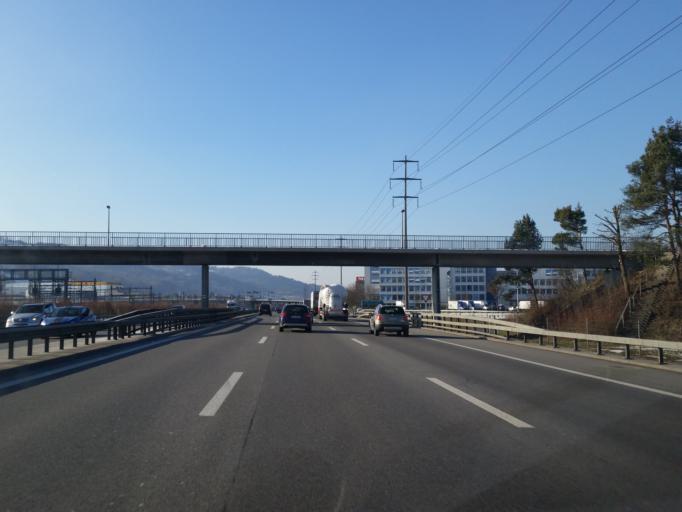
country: CH
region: Aargau
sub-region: Bezirk Baden
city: Spreitenbach
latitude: 47.4265
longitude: 8.3757
